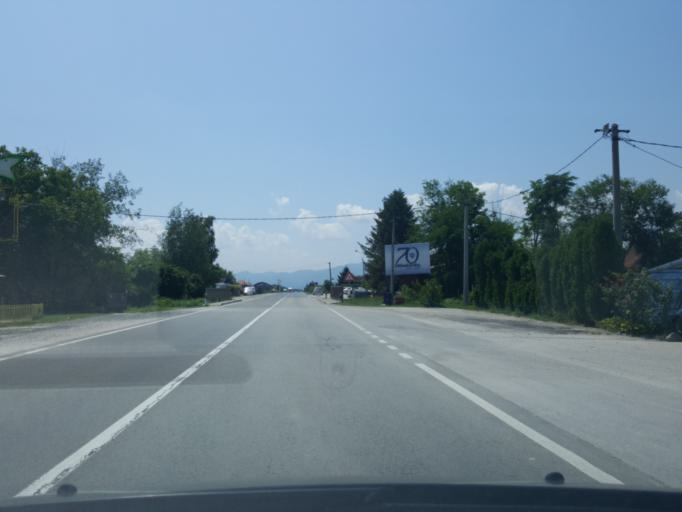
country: RS
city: Prislonica
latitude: 43.9293
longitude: 20.4105
